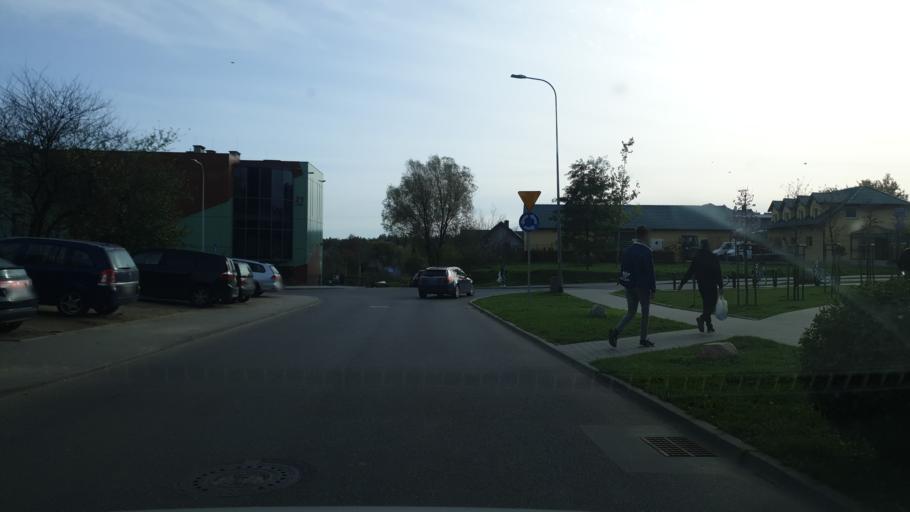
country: PL
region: Pomeranian Voivodeship
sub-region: Powiat gdanski
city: Kowale
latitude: 54.3496
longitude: 18.5902
